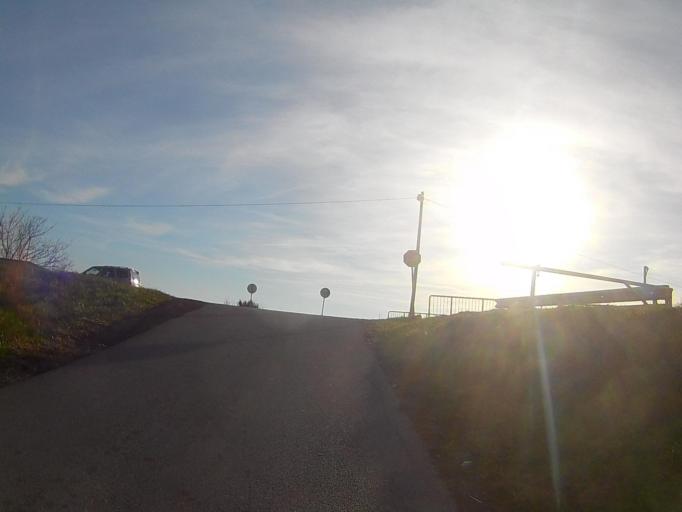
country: SI
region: Miklavz na Dravskem Polju
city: Miklavz na Dravskem Polju
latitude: 46.5260
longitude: 15.7031
